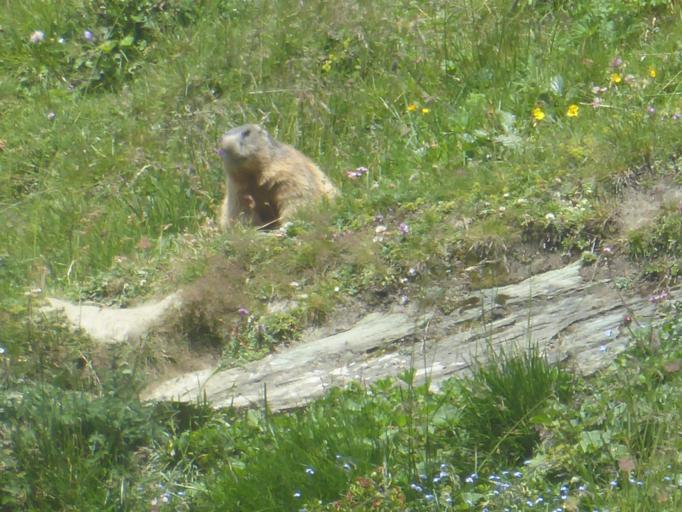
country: IT
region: Trentino-Alto Adige
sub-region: Bolzano
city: Predoi
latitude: 46.9821
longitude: 12.1228
